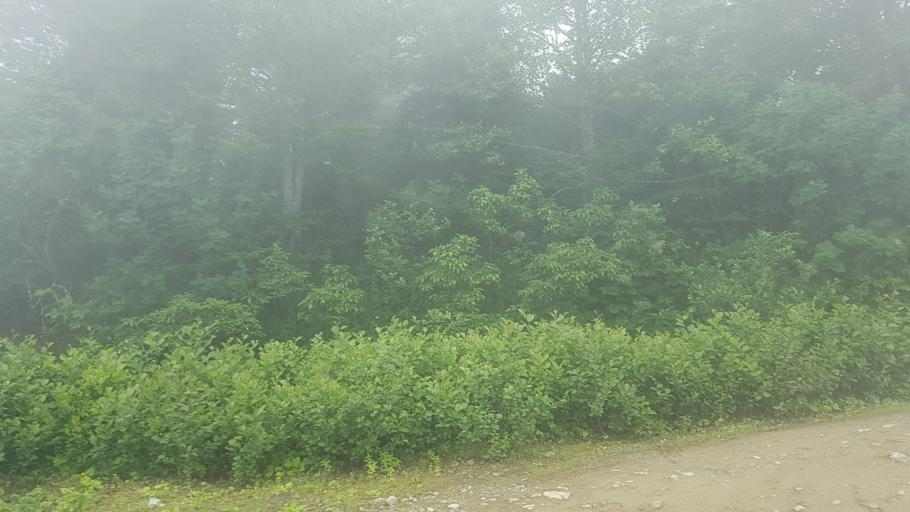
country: GE
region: Guria
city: Ozurgeti
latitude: 41.8397
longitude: 42.1438
